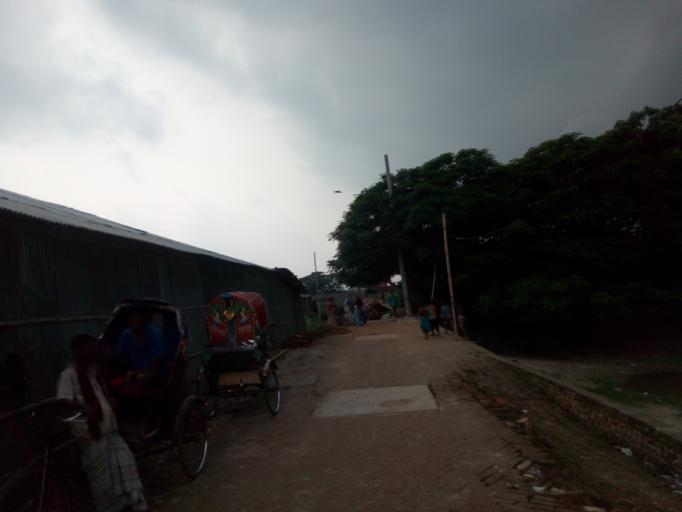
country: BD
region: Dhaka
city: Azimpur
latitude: 23.7384
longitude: 90.3589
